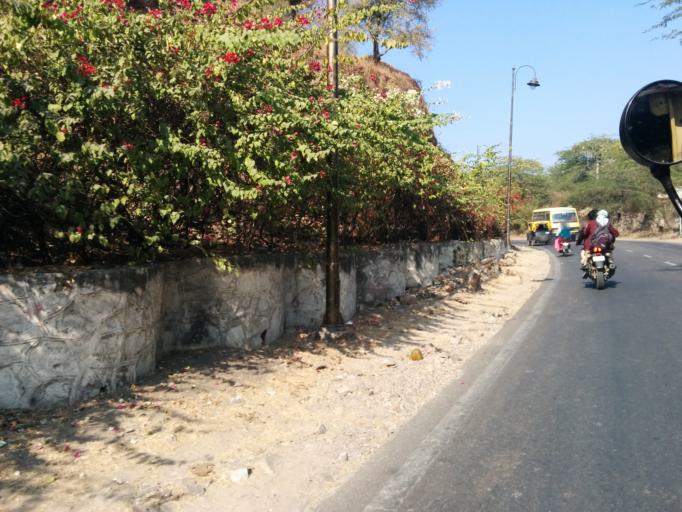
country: IN
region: Rajasthan
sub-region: Jaipur
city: Jaipur
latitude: 26.9643
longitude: 75.8467
